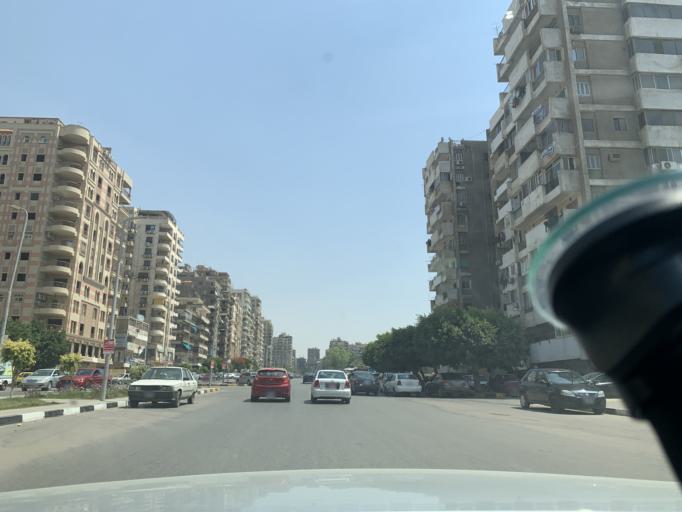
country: EG
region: Muhafazat al Qahirah
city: Cairo
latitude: 30.0661
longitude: 31.3490
